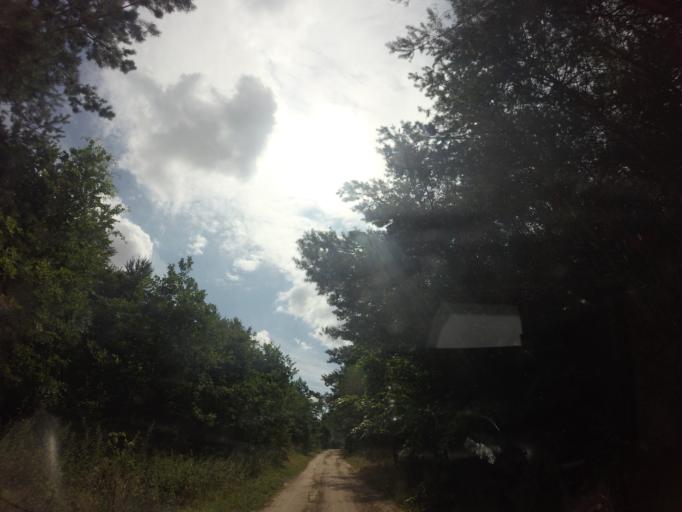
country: PL
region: West Pomeranian Voivodeship
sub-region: Powiat choszczenski
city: Drawno
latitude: 53.1980
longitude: 15.7698
